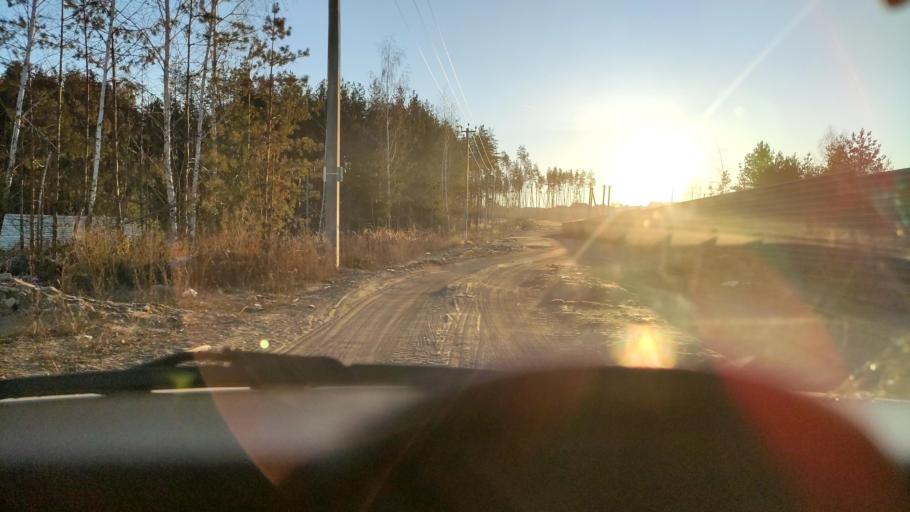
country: RU
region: Voronezj
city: Podgornoye
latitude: 51.7503
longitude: 39.1409
